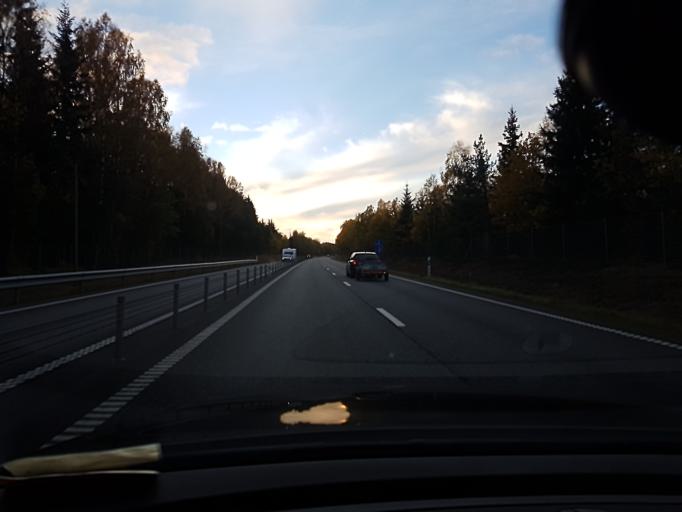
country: SE
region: Kronoberg
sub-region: Ljungby Kommun
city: Lagan
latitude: 56.8514
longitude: 14.0340
